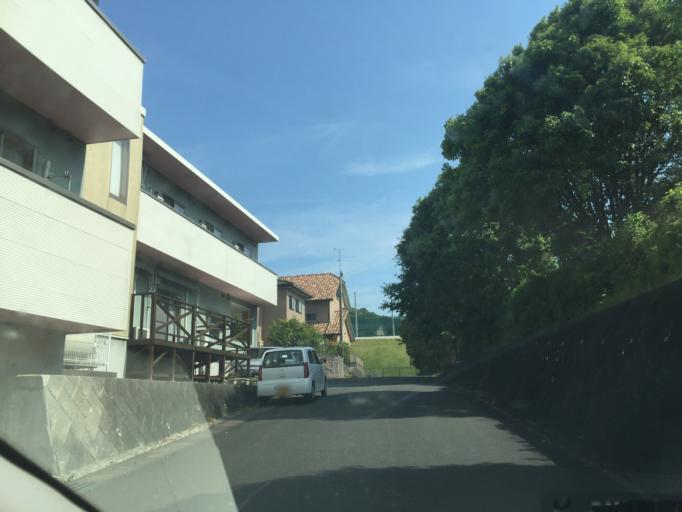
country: JP
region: Shizuoka
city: Kakegawa
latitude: 34.7633
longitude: 138.0251
